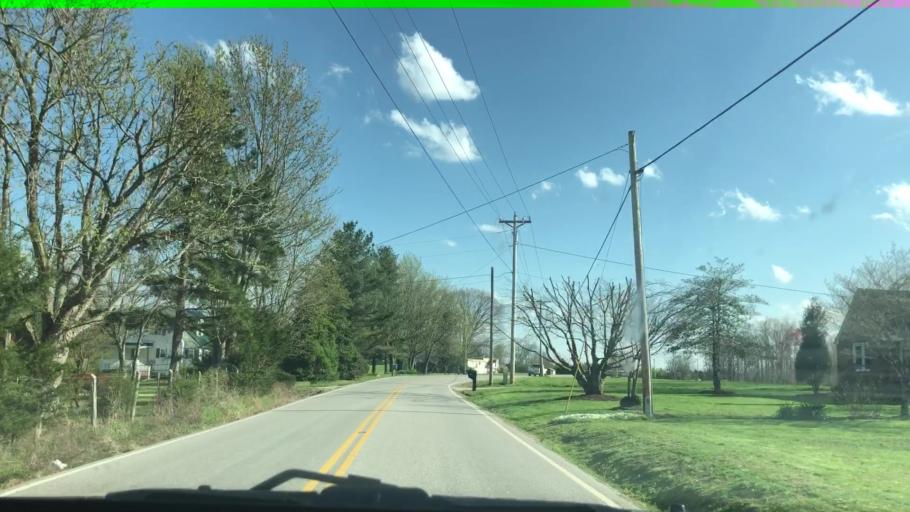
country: US
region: Tennessee
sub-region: Putnam County
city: Baxter
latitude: 36.0865
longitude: -85.5847
